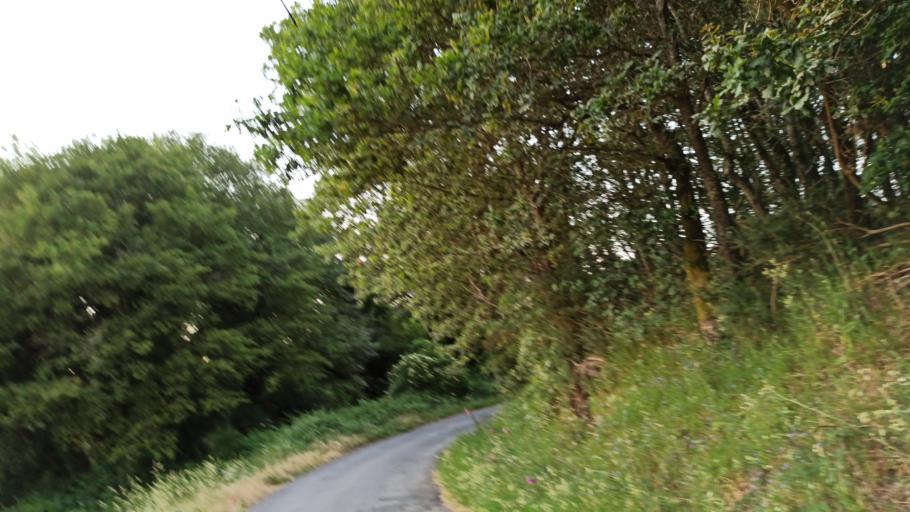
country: ES
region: Galicia
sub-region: Provincia da Coruna
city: Negreira
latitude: 42.9182
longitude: -8.7499
